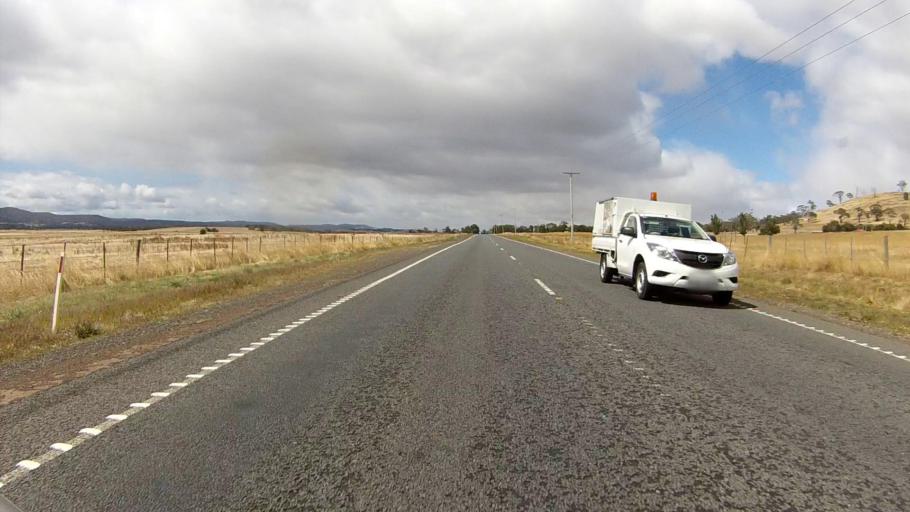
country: AU
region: Tasmania
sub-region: Northern Midlands
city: Evandale
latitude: -41.9746
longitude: 147.5031
